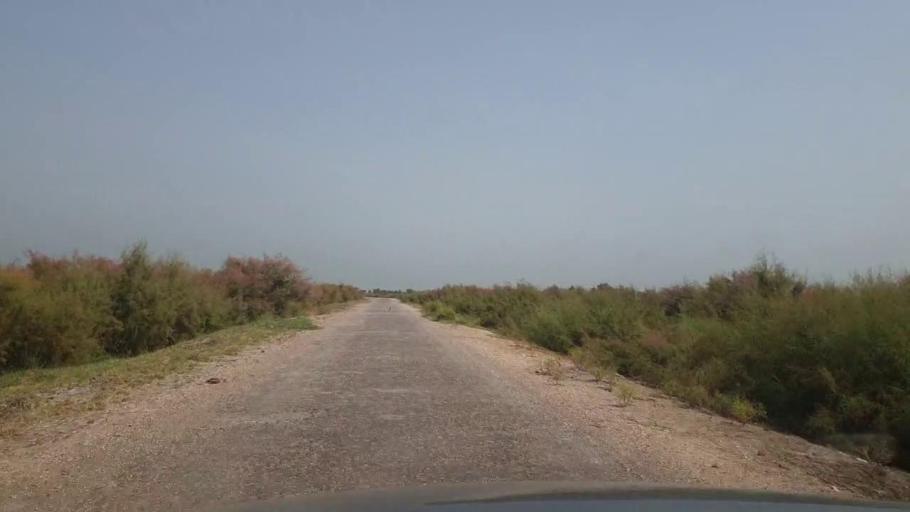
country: PK
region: Sindh
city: Madeji
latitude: 27.8308
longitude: 68.4469
